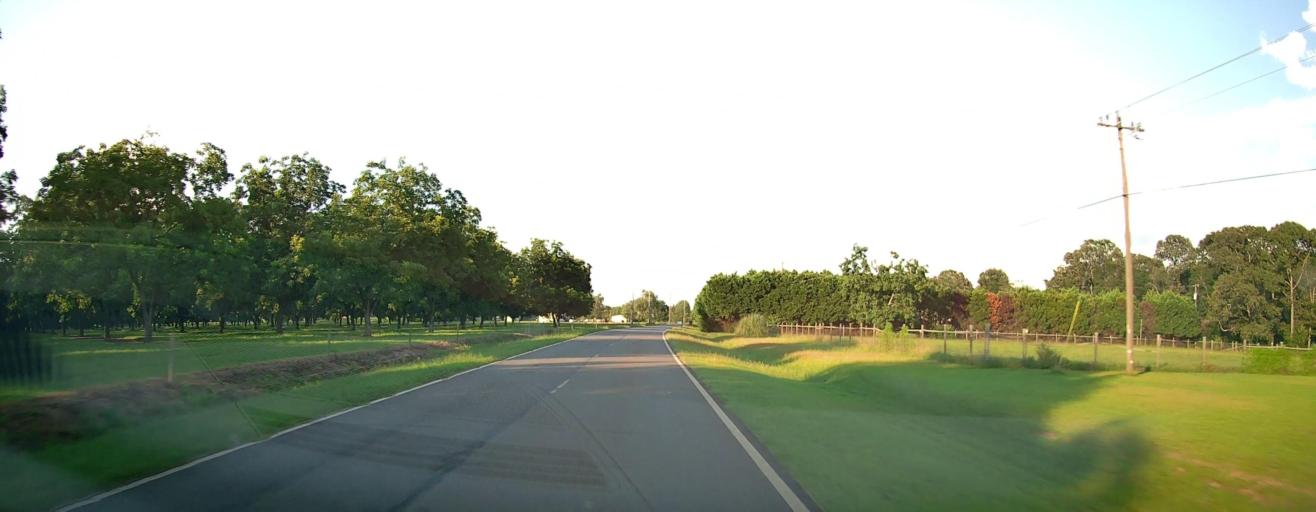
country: US
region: Georgia
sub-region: Peach County
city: Byron
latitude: 32.6314
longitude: -83.8113
